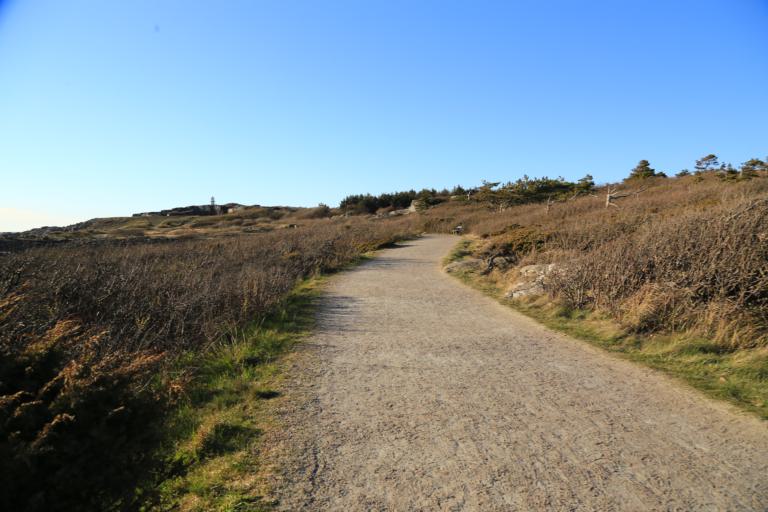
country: SE
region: Halland
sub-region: Varbergs Kommun
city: Varberg
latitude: 57.0854
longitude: 12.2409
